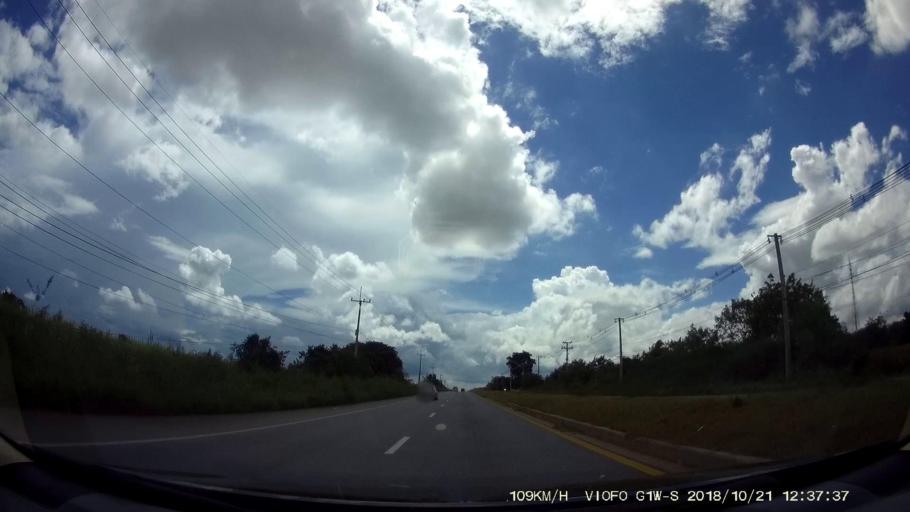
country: TH
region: Nakhon Ratchasima
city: Dan Khun Thot
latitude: 15.0662
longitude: 101.7104
